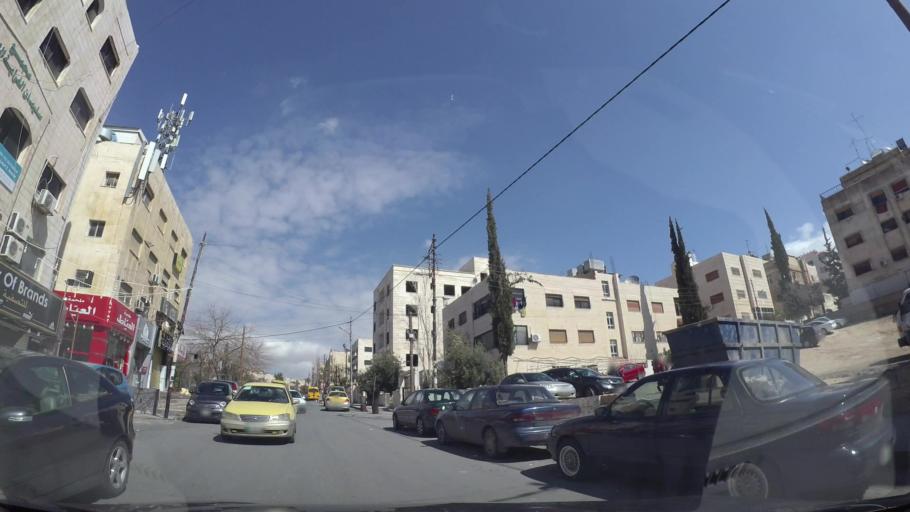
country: JO
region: Amman
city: Al Jubayhah
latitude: 31.9899
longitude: 35.9038
